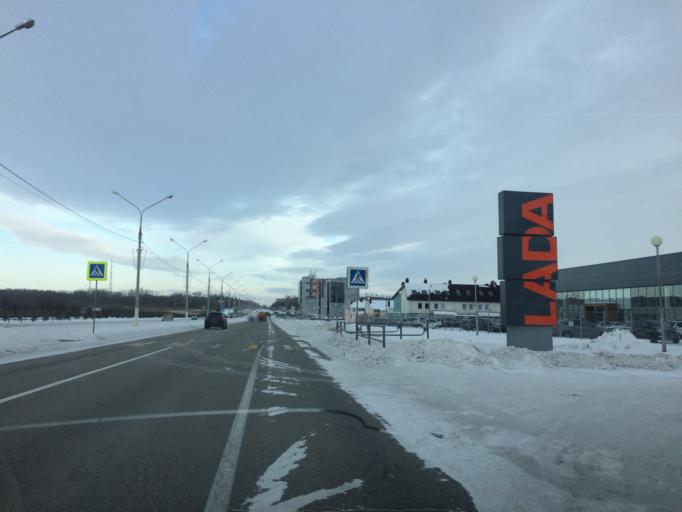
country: RU
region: Chelyabinsk
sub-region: Gorod Magnitogorsk
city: Magnitogorsk
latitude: 53.3833
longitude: 58.9619
